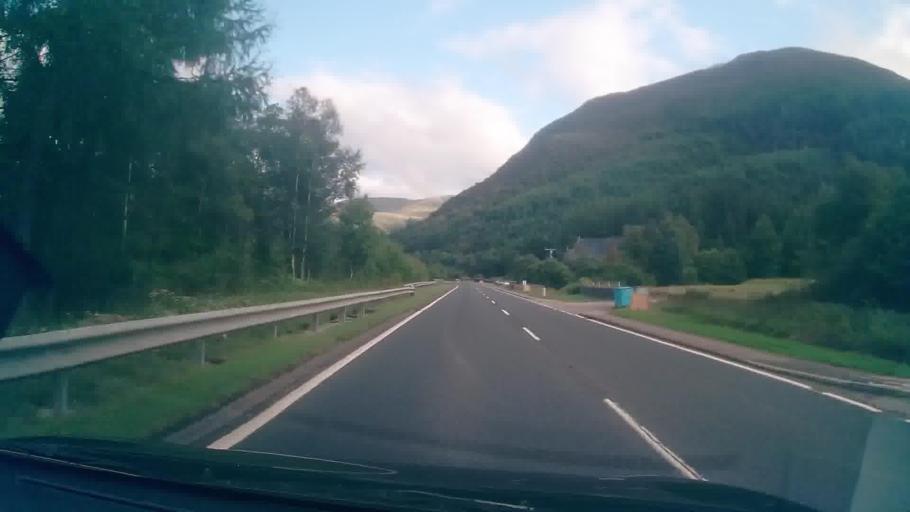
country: GB
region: Scotland
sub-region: Highland
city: Fort William
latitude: 56.6793
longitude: -5.1575
